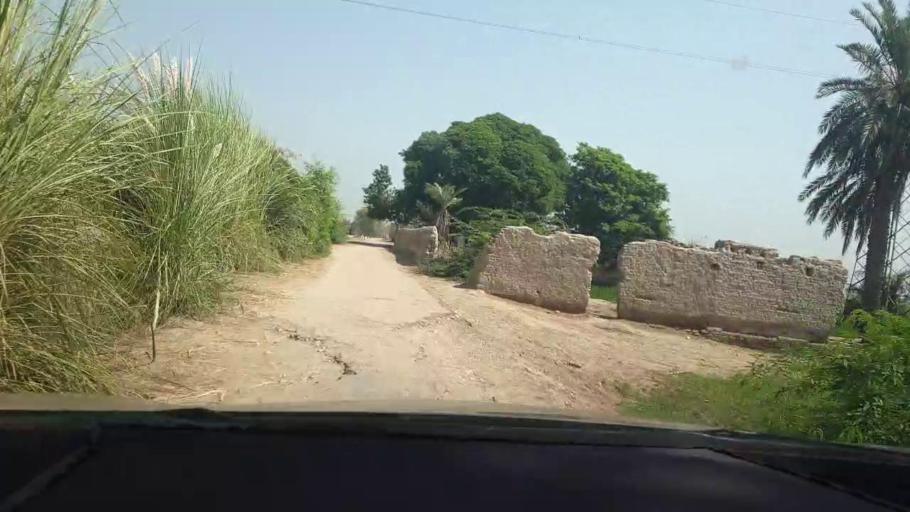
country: PK
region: Sindh
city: Kambar
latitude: 27.5880
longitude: 68.0614
